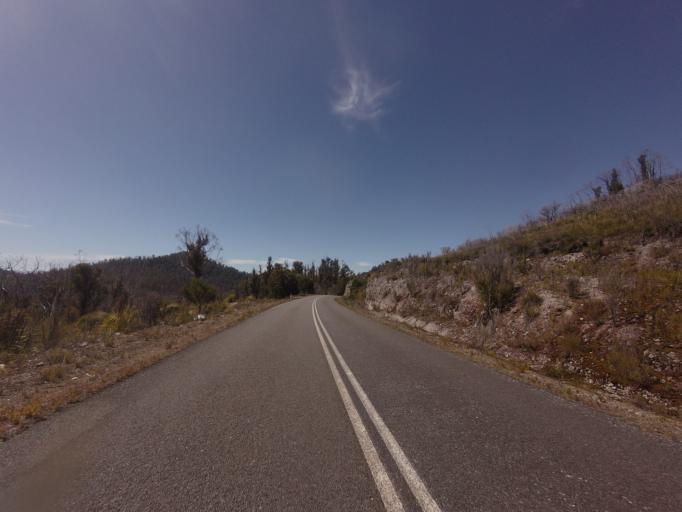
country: AU
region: Tasmania
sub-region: Huon Valley
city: Geeveston
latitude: -42.8500
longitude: 146.2358
